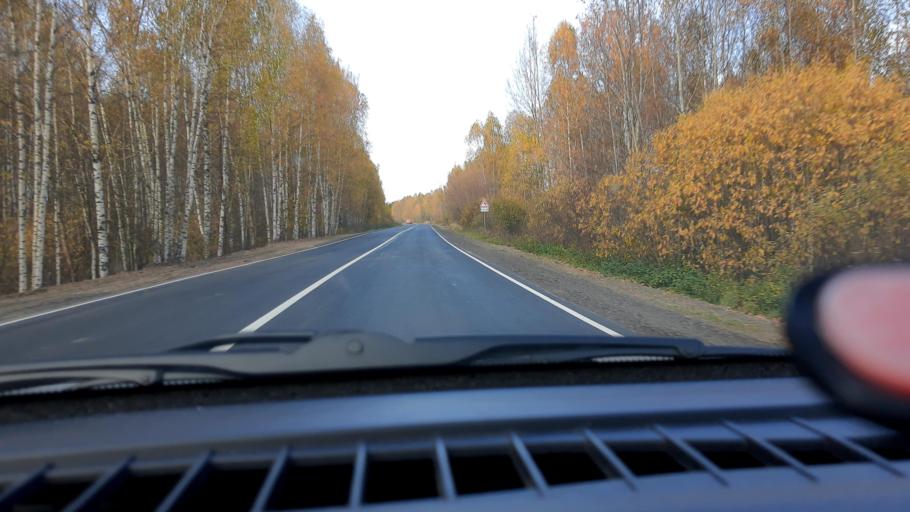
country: RU
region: Nizjnij Novgorod
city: Lukino
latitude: 56.5417
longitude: 43.7641
